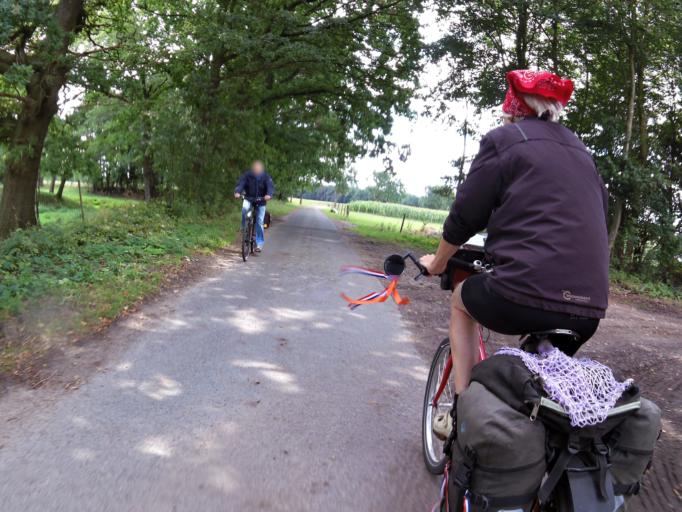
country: DE
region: Lower Saxony
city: Sandbostel
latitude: 53.3843
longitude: 9.1454
